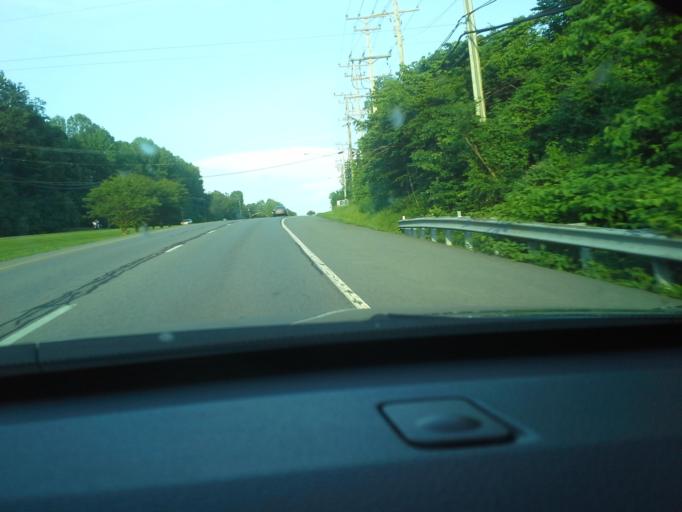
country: US
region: Maryland
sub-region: Calvert County
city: Chesapeake Beach
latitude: 38.6992
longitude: -76.5533
